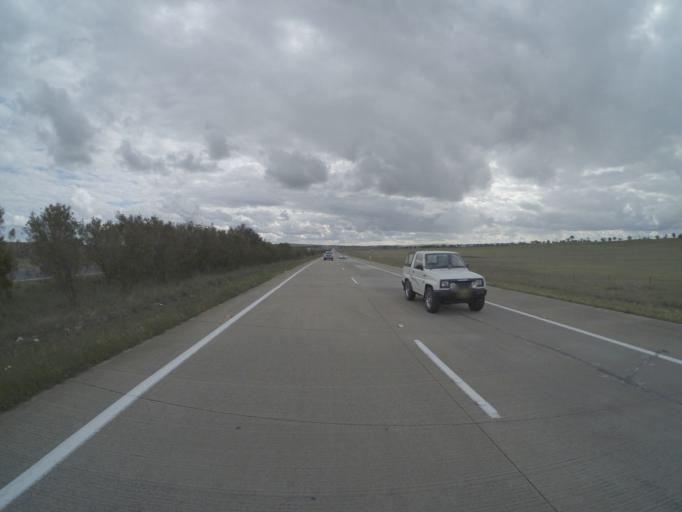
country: AU
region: New South Wales
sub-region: Goulburn Mulwaree
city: Goulburn
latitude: -34.8095
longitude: 149.5866
